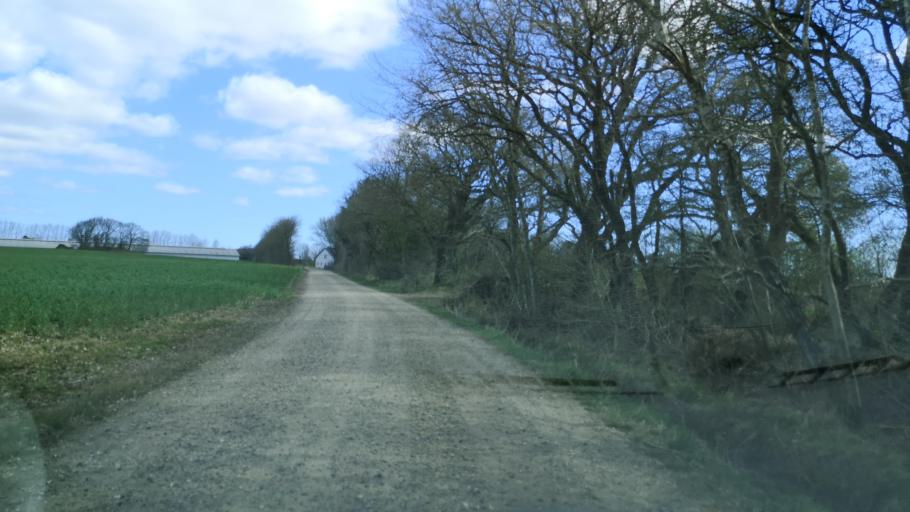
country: DK
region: Central Jutland
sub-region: Ringkobing-Skjern Kommune
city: Skjern
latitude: 55.9708
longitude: 8.5005
